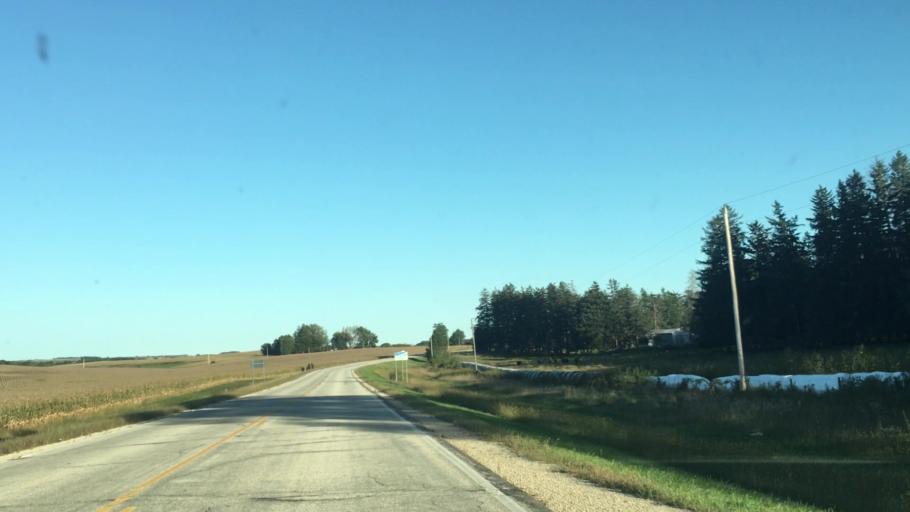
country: US
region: Minnesota
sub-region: Fillmore County
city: Chatfield
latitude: 43.8397
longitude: -92.0789
